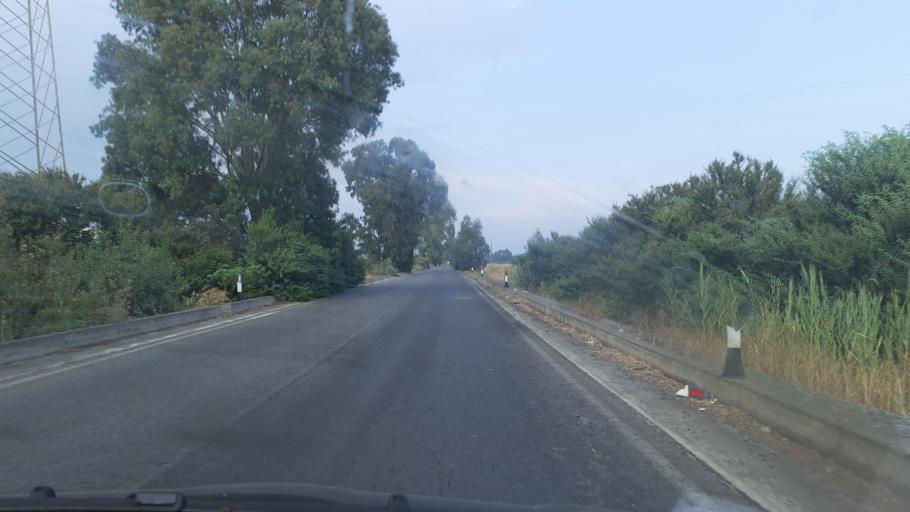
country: IT
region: Sicily
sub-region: Catania
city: Misterbianco
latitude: 37.4428
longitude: 15.0125
